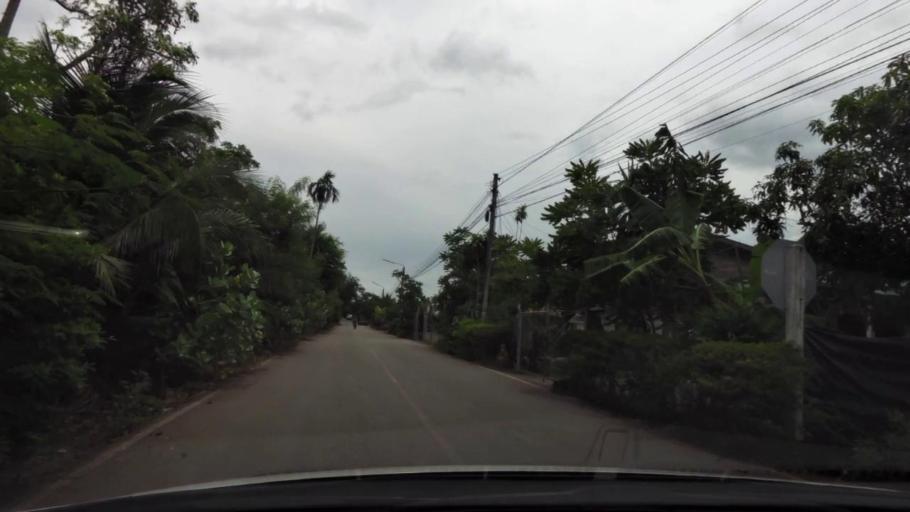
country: TH
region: Ratchaburi
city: Damnoen Saduak
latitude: 13.5490
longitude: 100.0184
